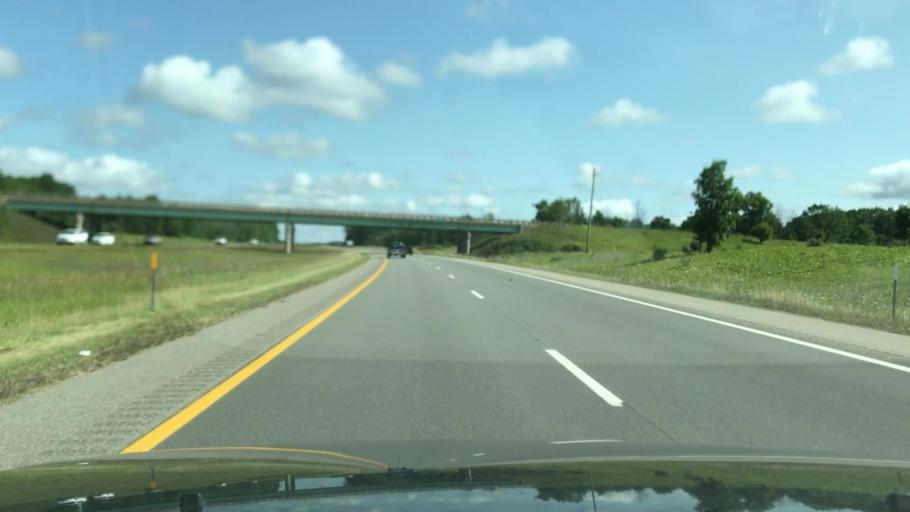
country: US
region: Michigan
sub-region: Montcalm County
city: Howard City
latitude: 43.3218
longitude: -85.5155
